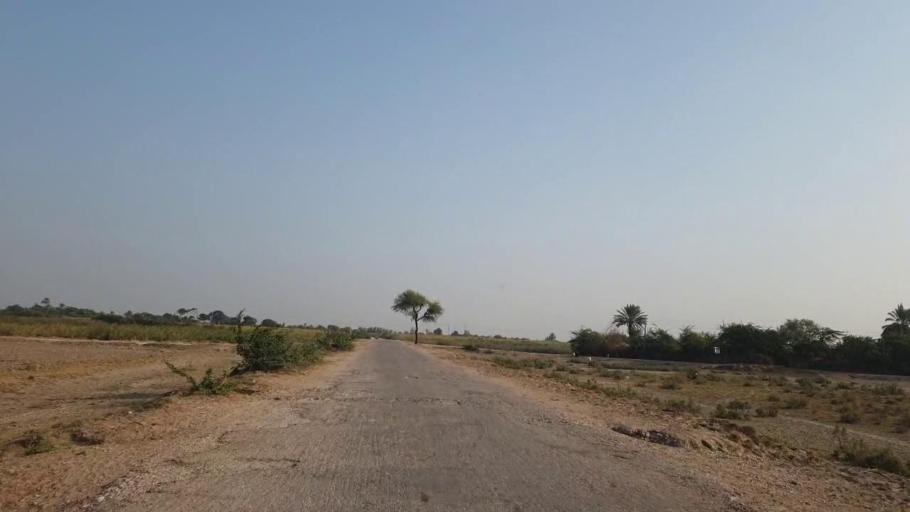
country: PK
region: Sindh
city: Bulri
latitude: 24.9718
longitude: 68.4041
